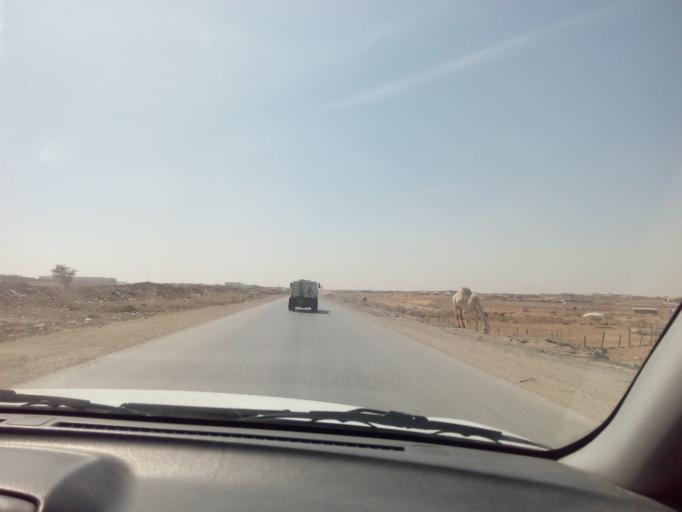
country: SA
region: Ar Riyad
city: Riyadh
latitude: 24.6382
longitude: 46.8798
